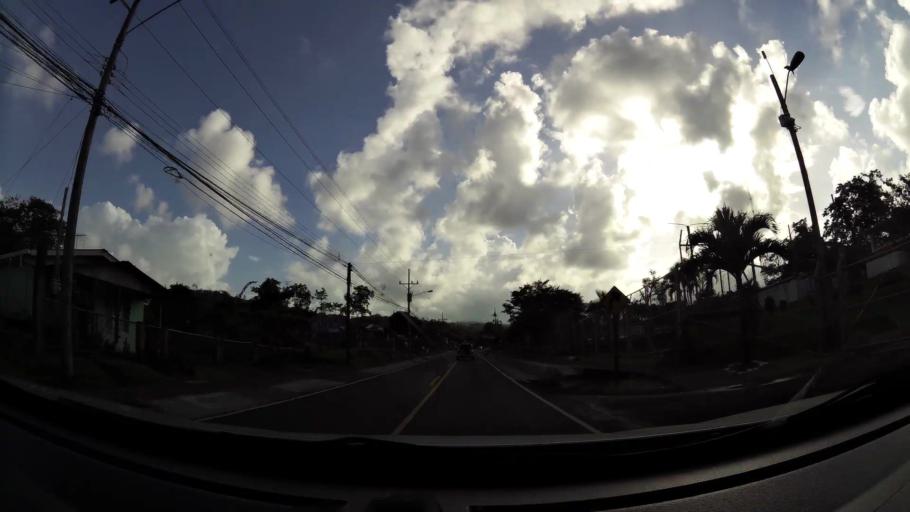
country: CR
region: Limon
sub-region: Canton de Siquirres
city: Siquirres
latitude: 10.0896
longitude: -83.5415
